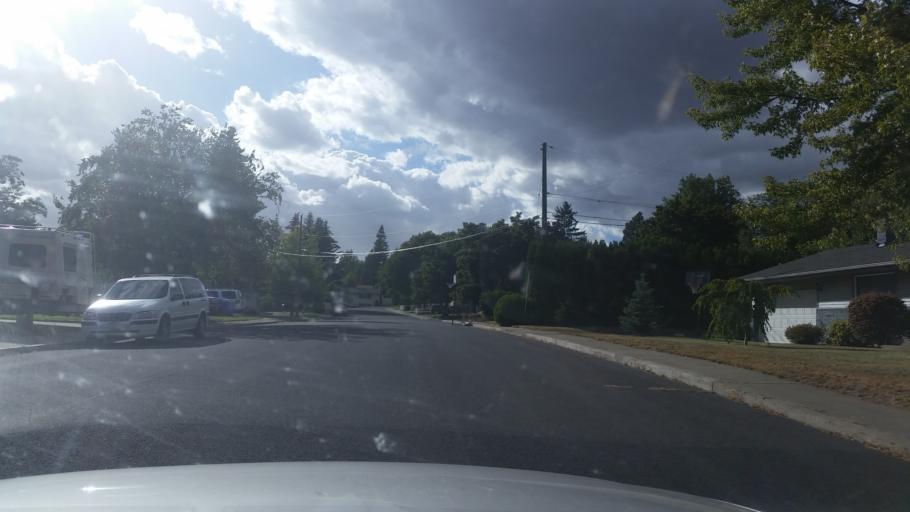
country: US
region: Washington
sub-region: Spokane County
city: Cheney
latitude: 47.4826
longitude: -117.5943
